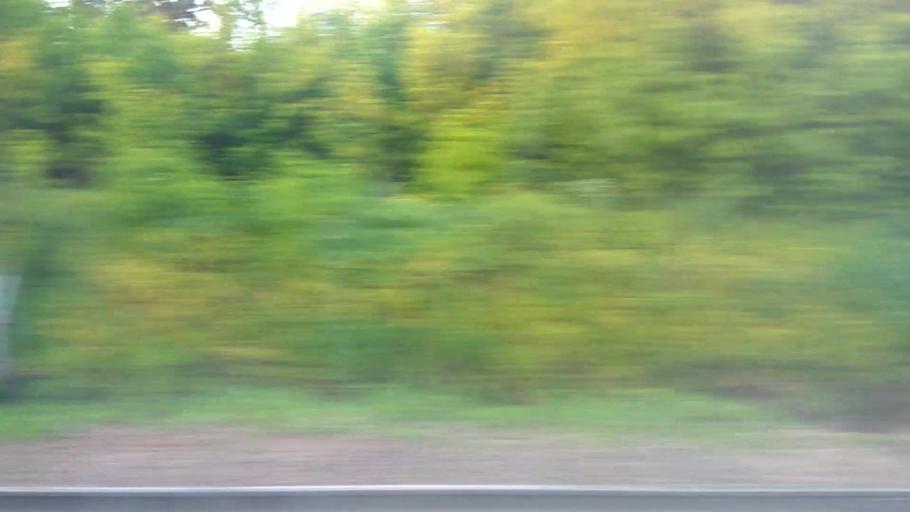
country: RU
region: Moskovskaya
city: Barybino
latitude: 55.2742
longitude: 37.8943
